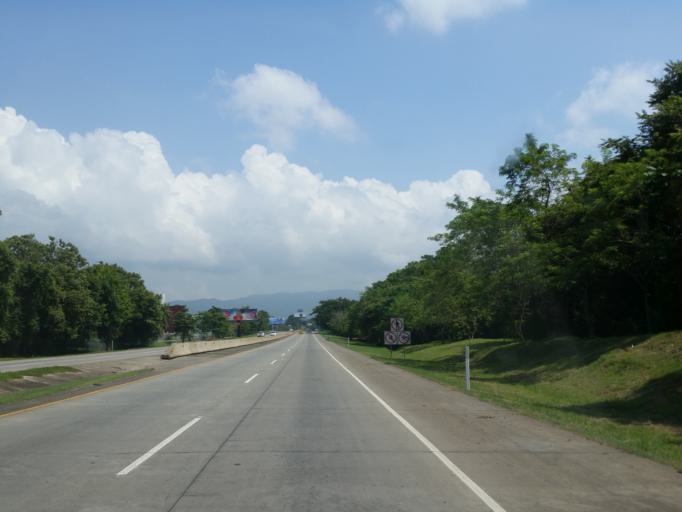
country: PA
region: Panama
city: Tocumen
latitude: 9.0608
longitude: -79.4029
